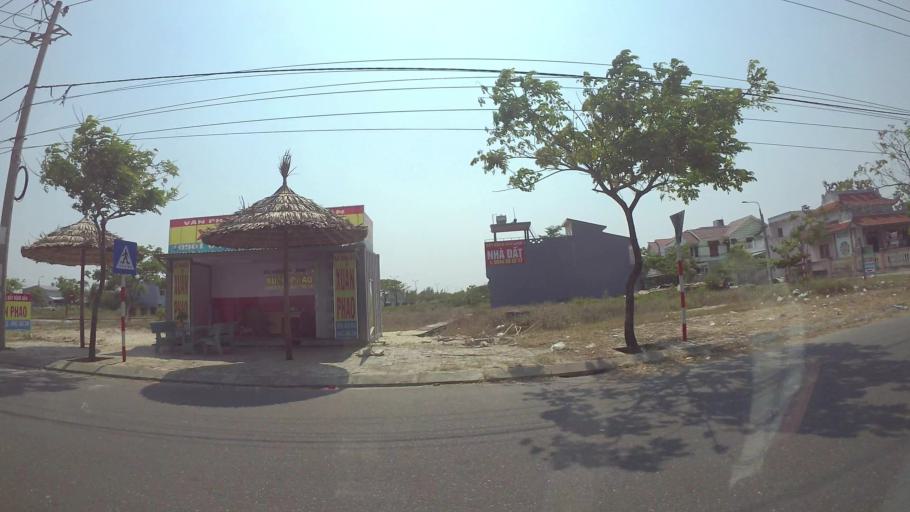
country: VN
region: Da Nang
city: Ngu Hanh Son
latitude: 15.9861
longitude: 108.2701
